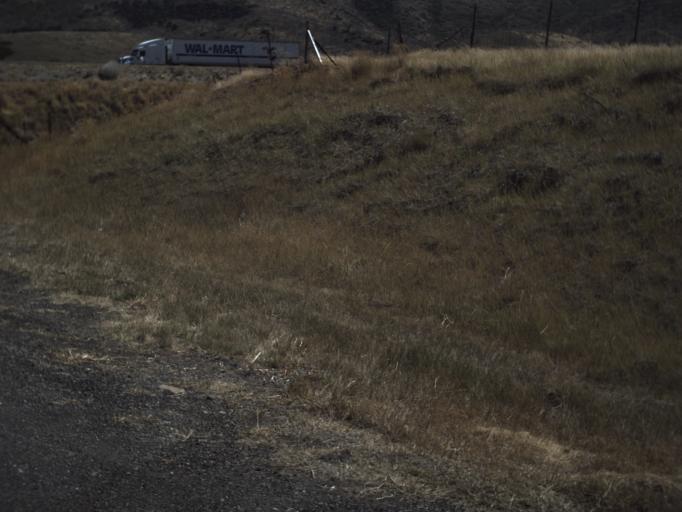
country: US
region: Utah
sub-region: Beaver County
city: Beaver
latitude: 38.6597
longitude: -112.5953
